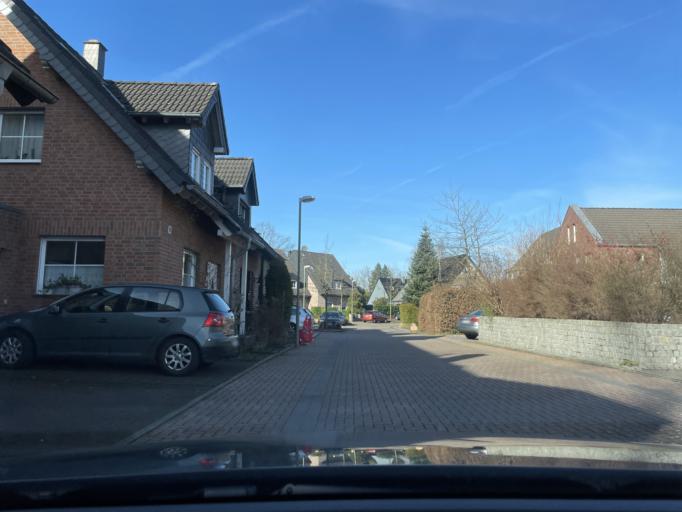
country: DE
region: North Rhine-Westphalia
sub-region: Regierungsbezirk Dusseldorf
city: Neuss
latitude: 51.2101
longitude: 6.6604
